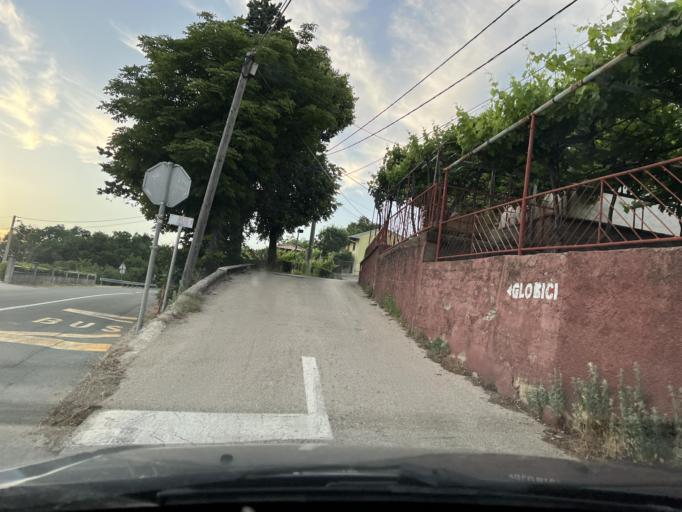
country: HR
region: Primorsko-Goranska
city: Marcelji
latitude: 45.3930
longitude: 14.4017
